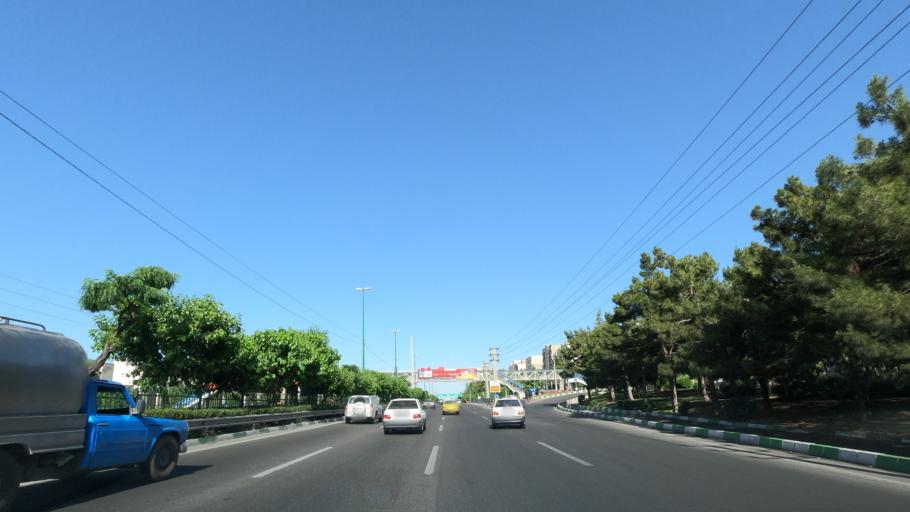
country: IR
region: Tehran
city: Tehran
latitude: 35.7533
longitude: 51.3051
